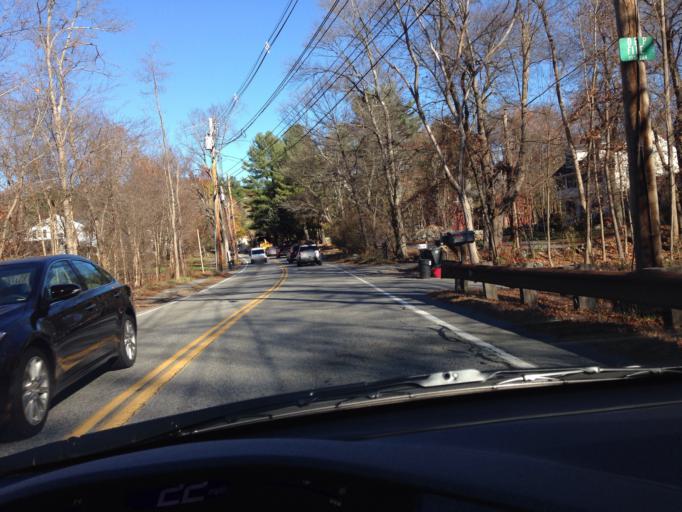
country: US
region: Massachusetts
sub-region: Middlesex County
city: Bedford
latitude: 42.4948
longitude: -71.2578
